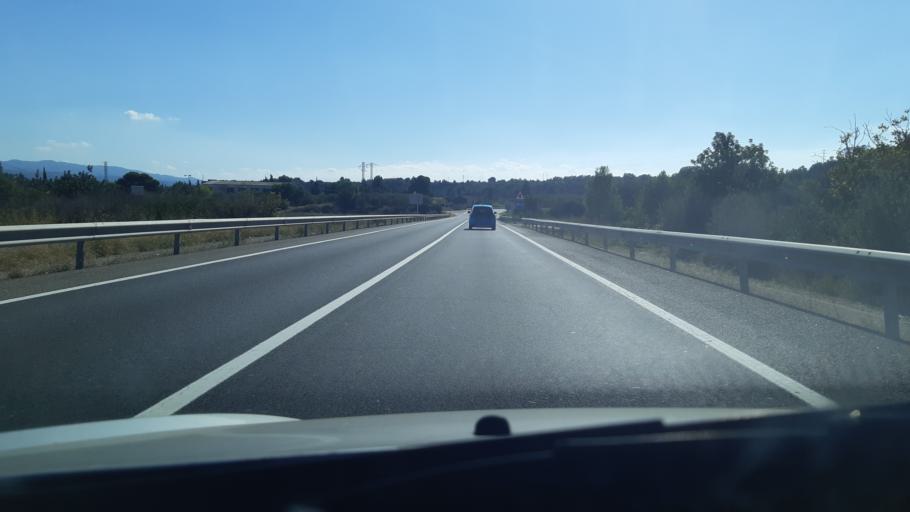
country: ES
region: Catalonia
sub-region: Provincia de Tarragona
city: Tivenys
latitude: 40.9074
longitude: 0.4832
